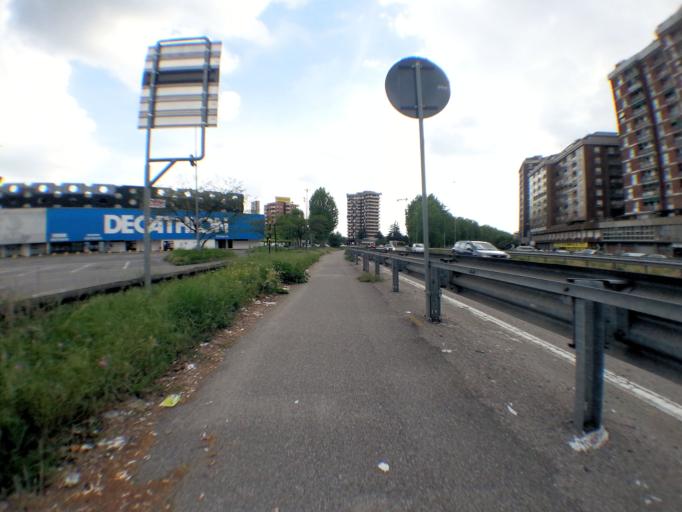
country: IT
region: Lombardy
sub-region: Citta metropolitana di Milano
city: Sesto San Giovanni
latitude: 45.5506
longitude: 9.2380
